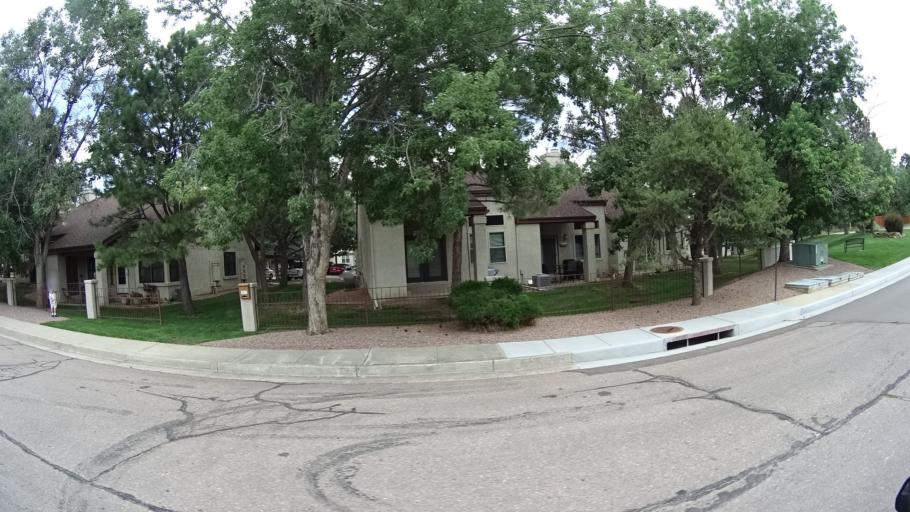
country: US
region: Colorado
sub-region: El Paso County
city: Colorado Springs
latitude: 38.9047
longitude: -104.8367
